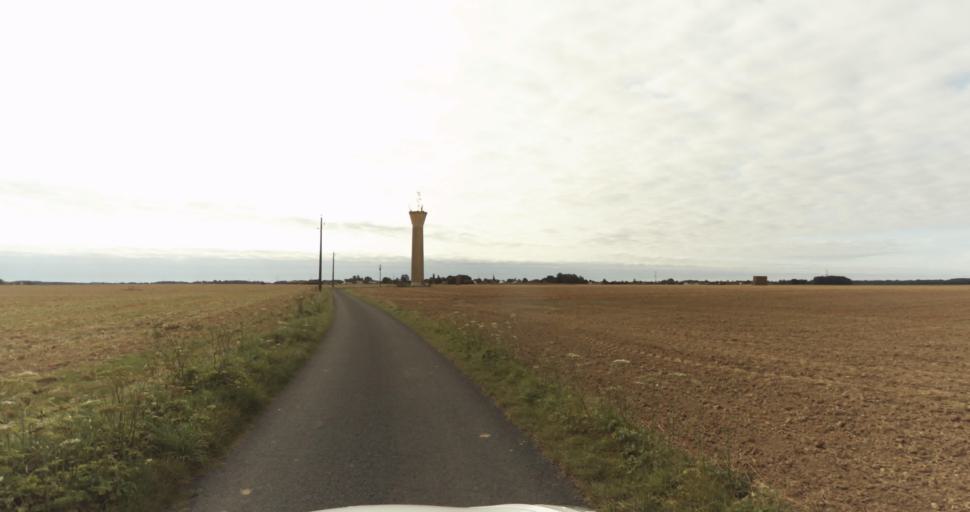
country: FR
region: Haute-Normandie
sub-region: Departement de l'Eure
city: La Madeleine-de-Nonancourt
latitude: 48.8736
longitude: 1.2374
